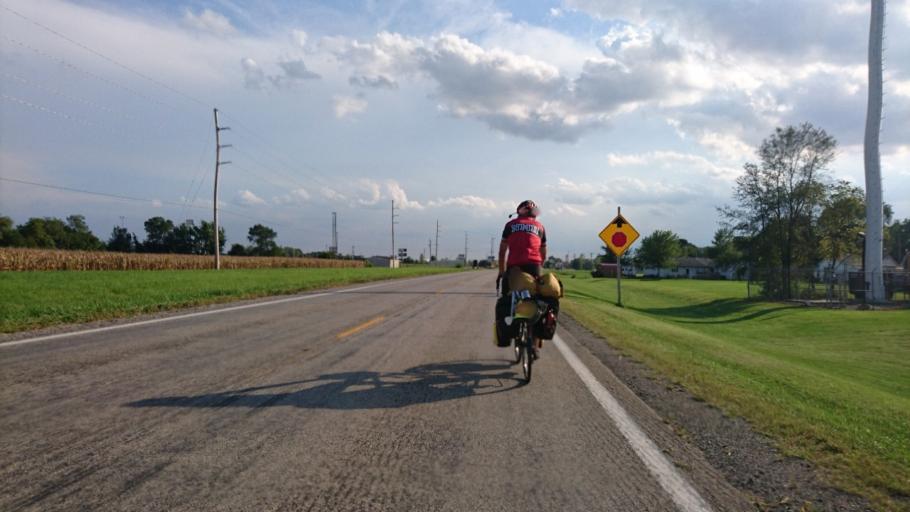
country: US
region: Illinois
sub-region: Logan County
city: Atlanta
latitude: 40.2623
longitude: -89.2240
